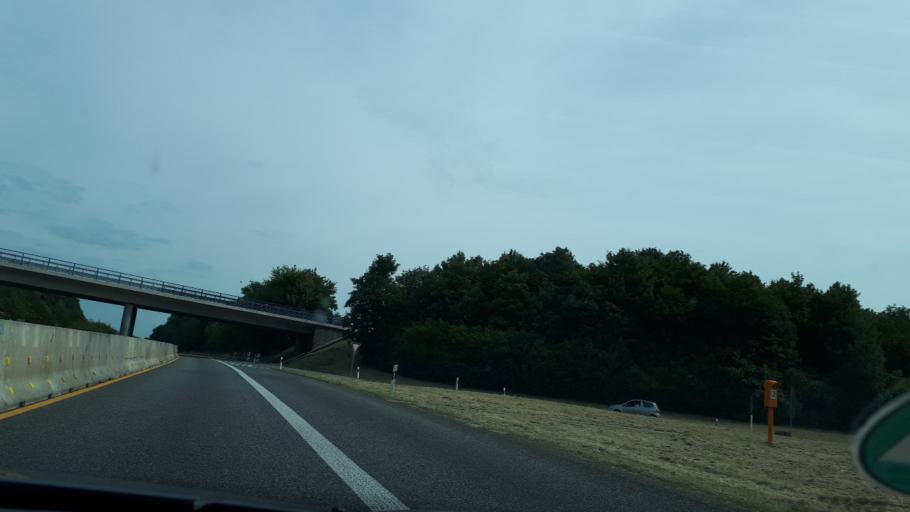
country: DE
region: Rheinland-Pfalz
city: Kaifenheim
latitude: 50.2433
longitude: 7.2165
